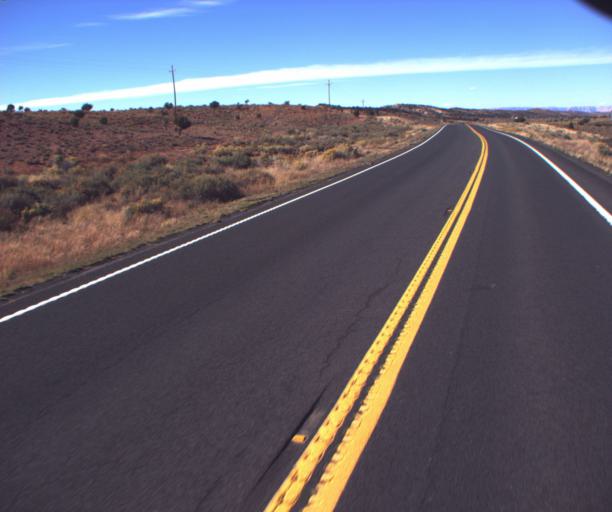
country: US
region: Arizona
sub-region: Coconino County
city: Tuba City
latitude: 36.3954
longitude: -111.5266
